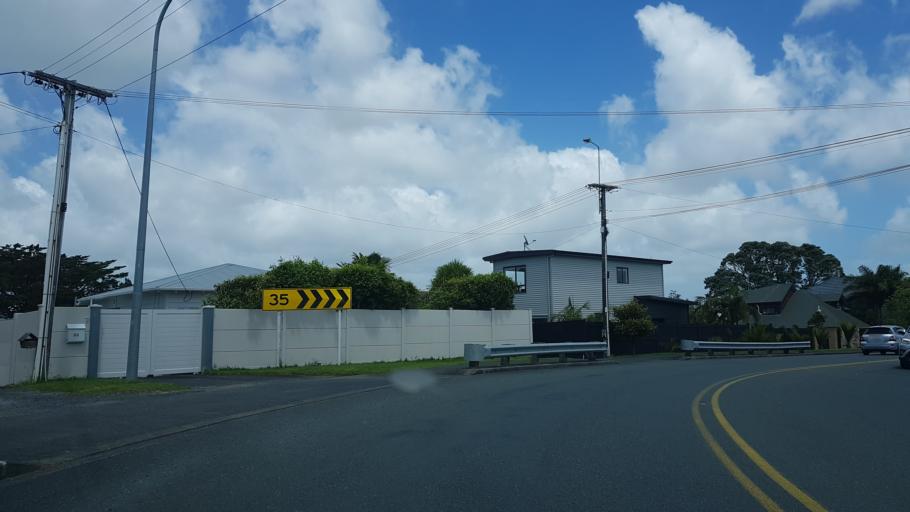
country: NZ
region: Auckland
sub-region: Auckland
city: North Shore
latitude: -36.8091
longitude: 174.7015
